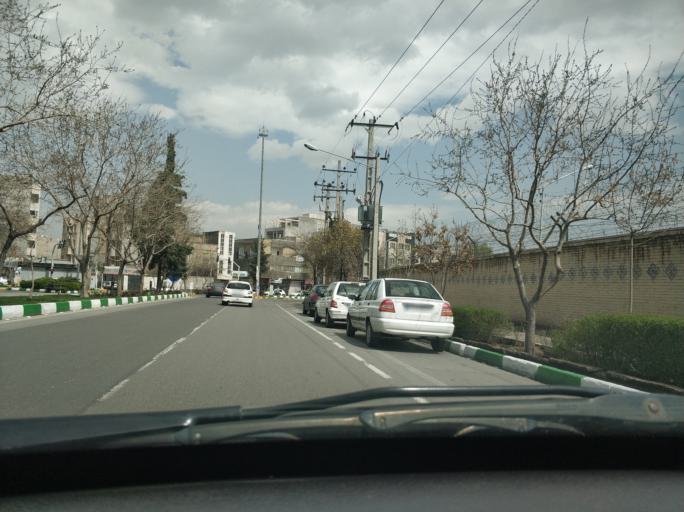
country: IR
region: Razavi Khorasan
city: Mashhad
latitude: 36.2838
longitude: 59.5780
